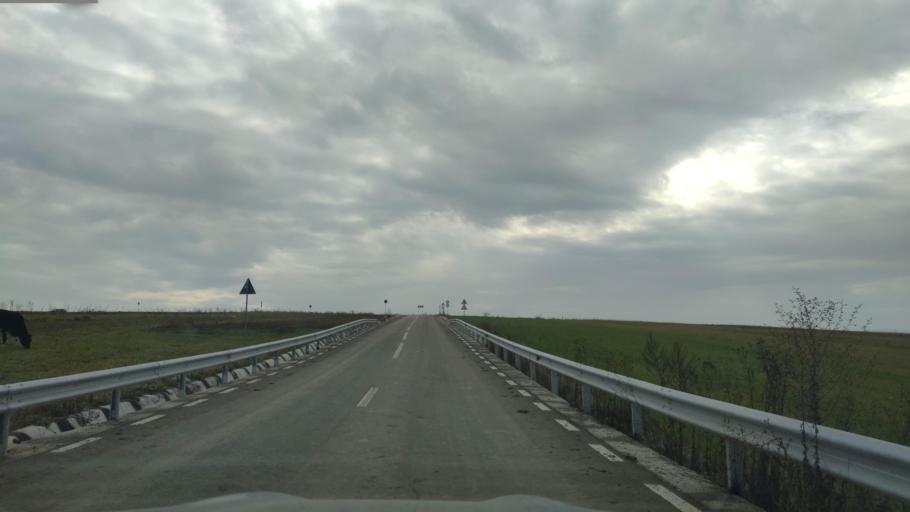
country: RO
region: Harghita
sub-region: Comuna Subcetate
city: Subcetate
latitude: 46.8192
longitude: 25.4477
